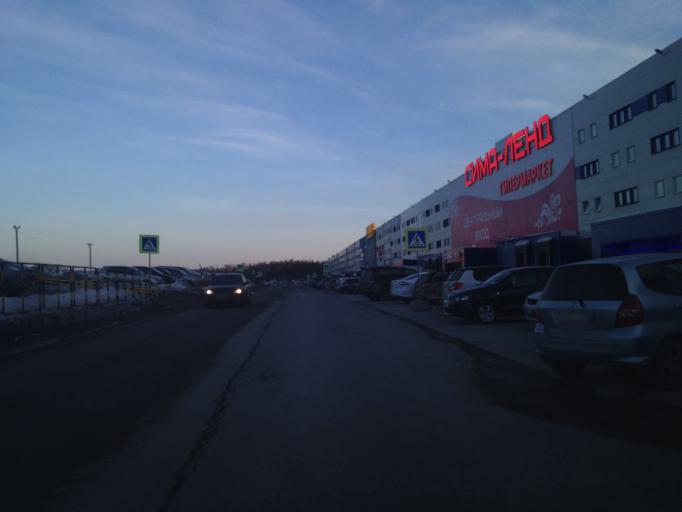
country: RU
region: Sverdlovsk
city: Istok
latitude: 56.7617
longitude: 60.7506
